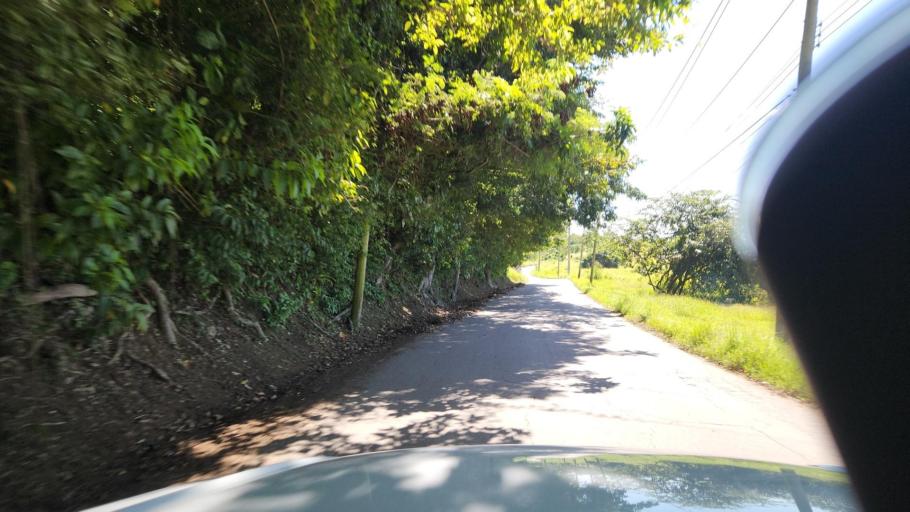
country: BB
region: Saint Thomas
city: Welchman Hall
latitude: 13.1883
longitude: -59.5958
